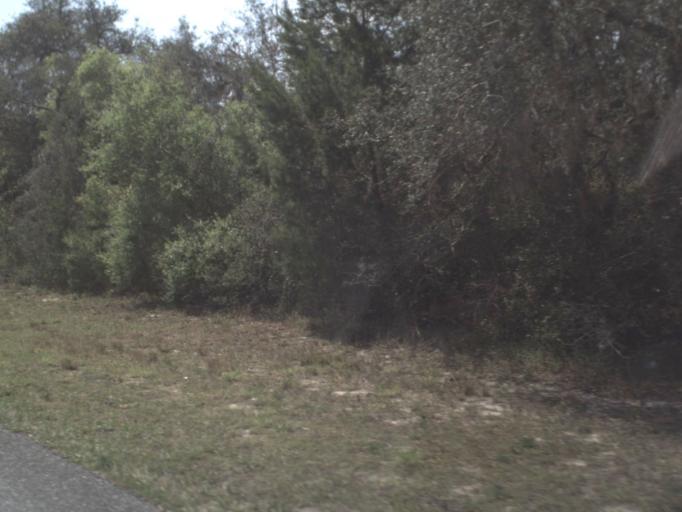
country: US
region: Florida
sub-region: Lake County
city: Astor
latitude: 29.1241
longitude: -81.6193
